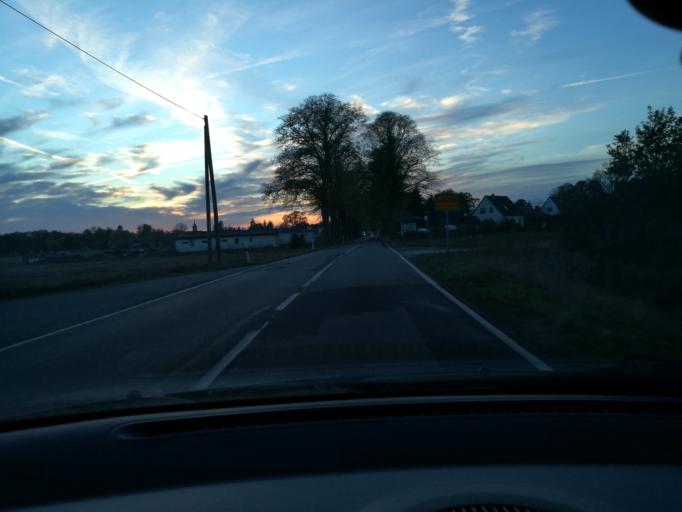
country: DE
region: Brandenburg
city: Lenzen
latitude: 53.0944
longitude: 11.4899
